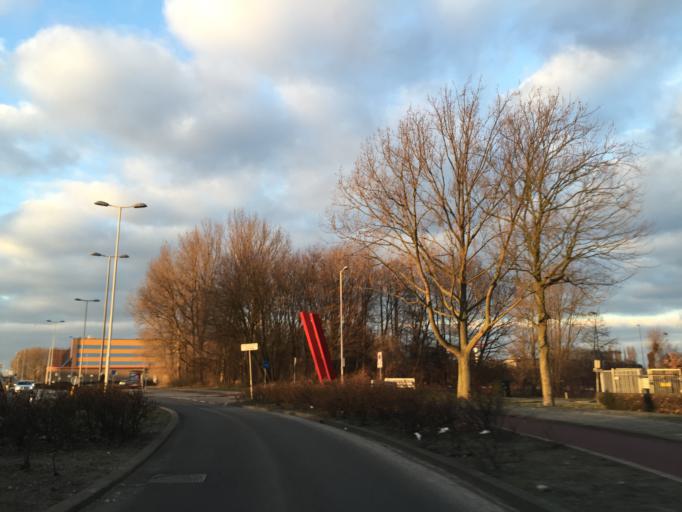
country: NL
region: South Holland
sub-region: Gemeente Rotterdam
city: Delfshaven
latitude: 51.9225
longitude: 4.4375
